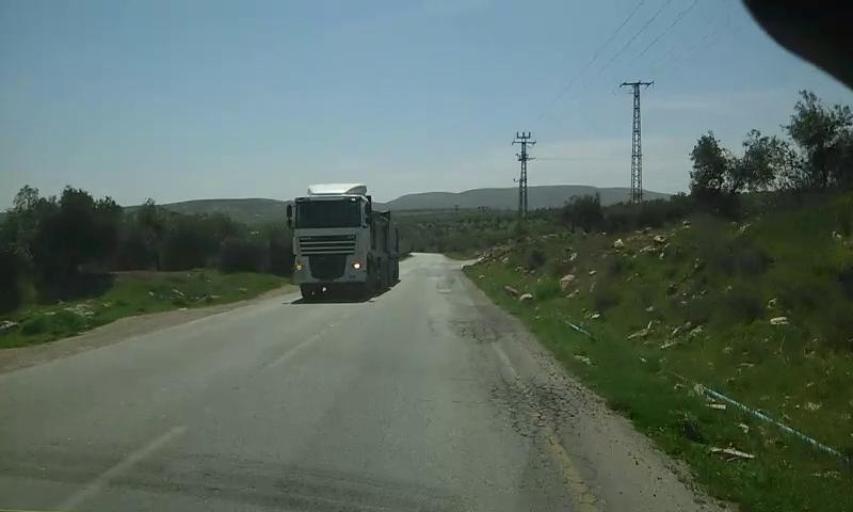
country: PS
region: West Bank
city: Marah Rabbah
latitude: 31.6339
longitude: 35.2028
